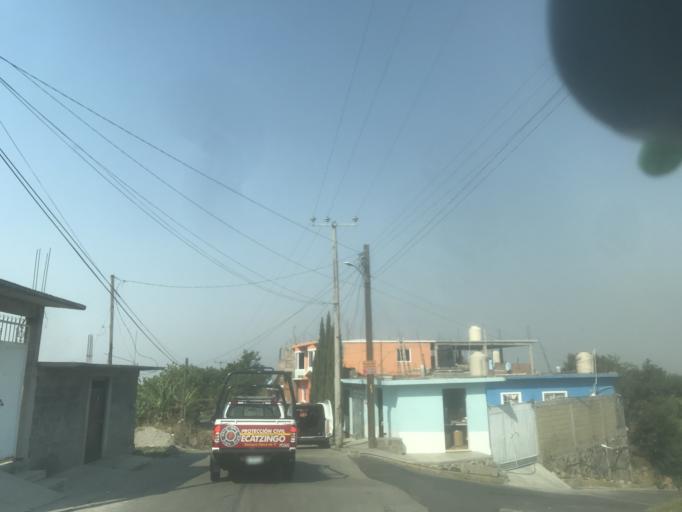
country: MX
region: Mexico
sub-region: Ecatzingo
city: San Juan Tlacotompa (Tlacotompa)
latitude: 18.9398
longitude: -98.7931
